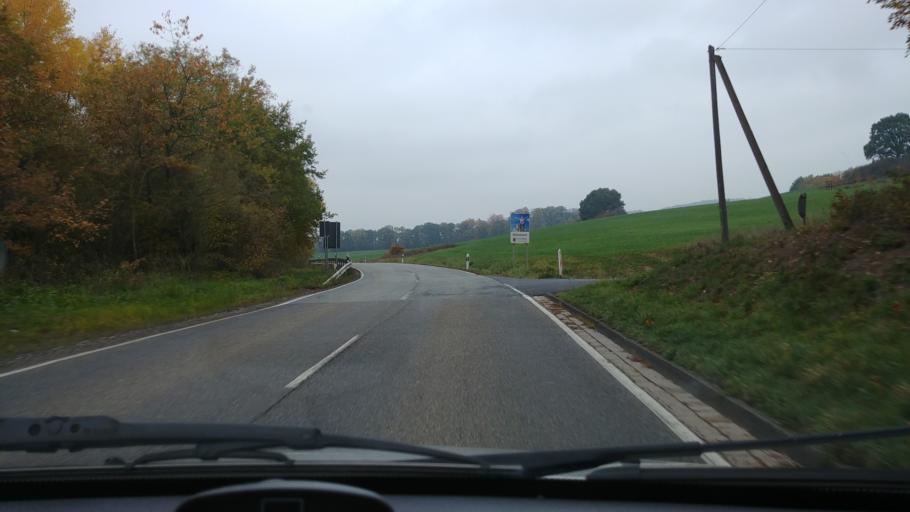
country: DE
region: Rheinland-Pfalz
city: Gemunden
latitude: 50.5427
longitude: 8.0258
